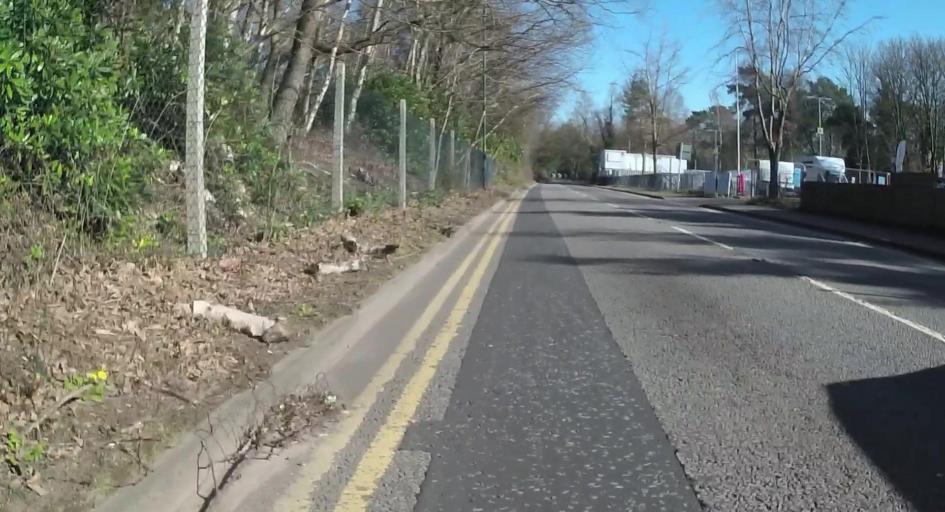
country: GB
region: England
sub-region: Royal Borough of Windsor and Maidenhead
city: Ascot
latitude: 51.4063
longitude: -0.6738
